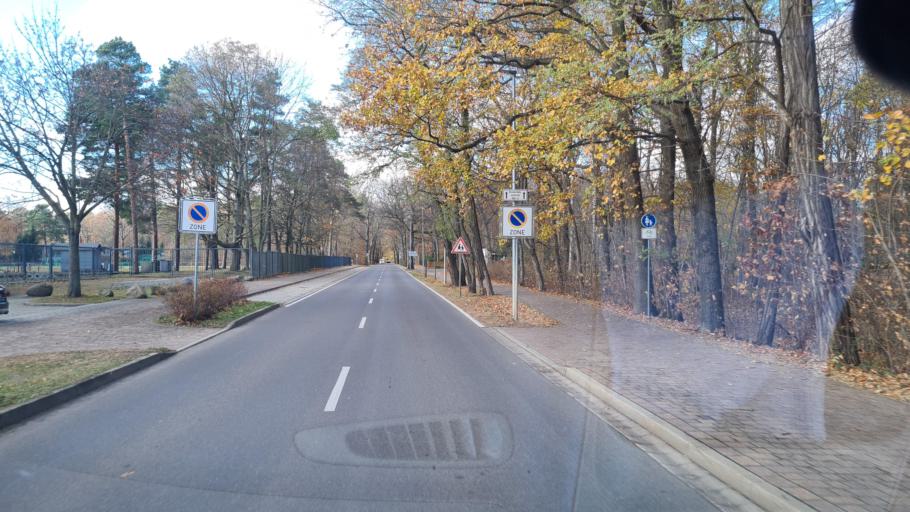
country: DE
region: Brandenburg
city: Spremberg
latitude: 51.5742
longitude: 14.3611
